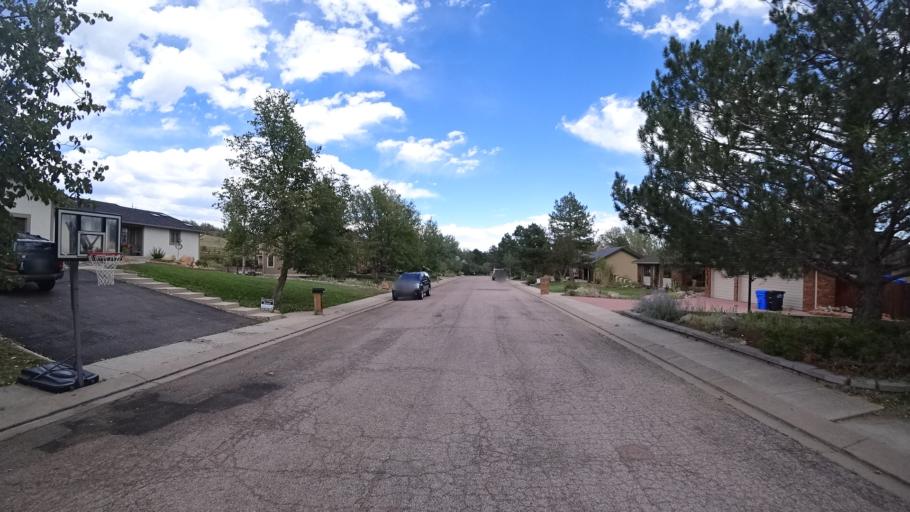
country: US
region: Colorado
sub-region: El Paso County
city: Stratmoor
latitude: 38.7793
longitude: -104.8334
